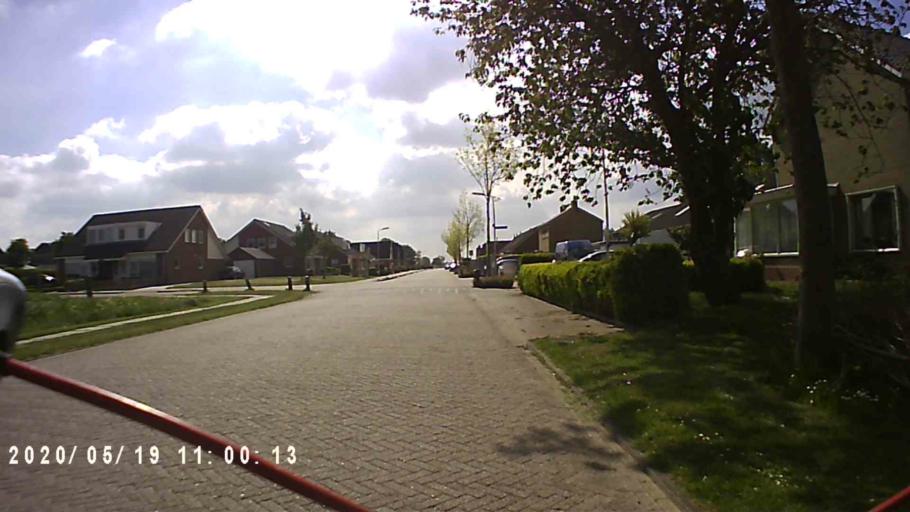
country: NL
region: Groningen
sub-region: Gemeente Zuidhorn
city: Grijpskerk
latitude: 53.3045
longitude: 6.2679
